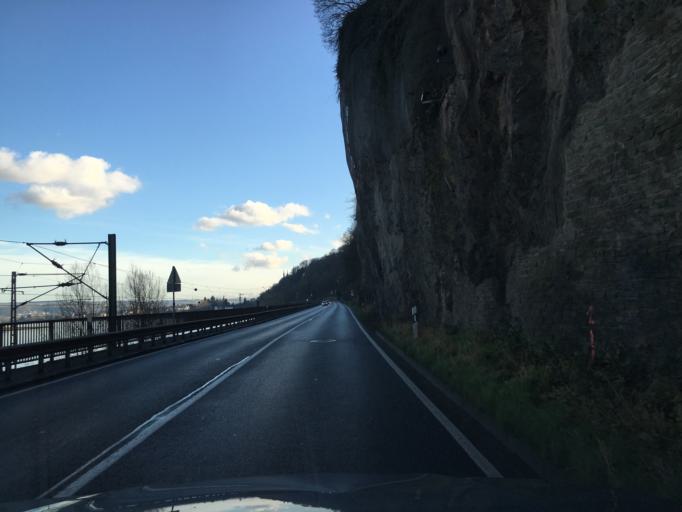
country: DE
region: Rheinland-Pfalz
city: Unkel
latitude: 50.5893
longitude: 7.2106
